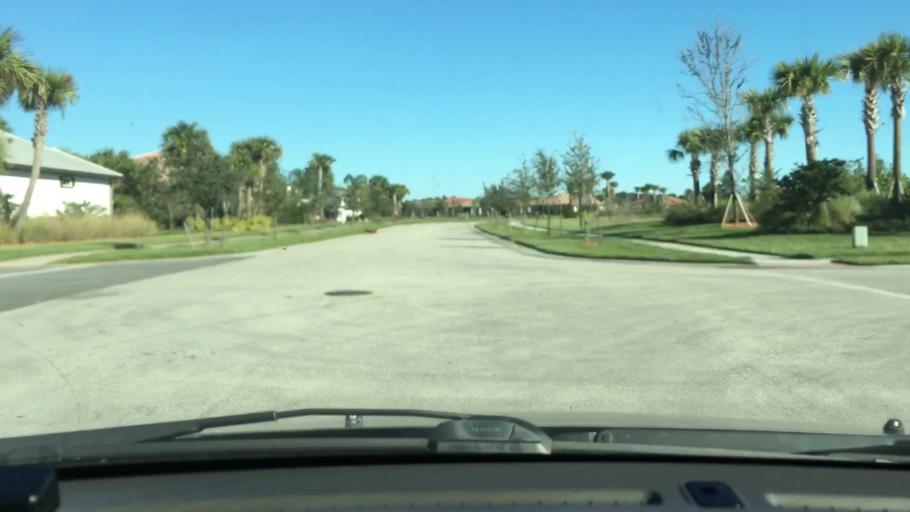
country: US
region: Florida
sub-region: Indian River County
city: Gifford
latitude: 27.6876
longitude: -80.4320
